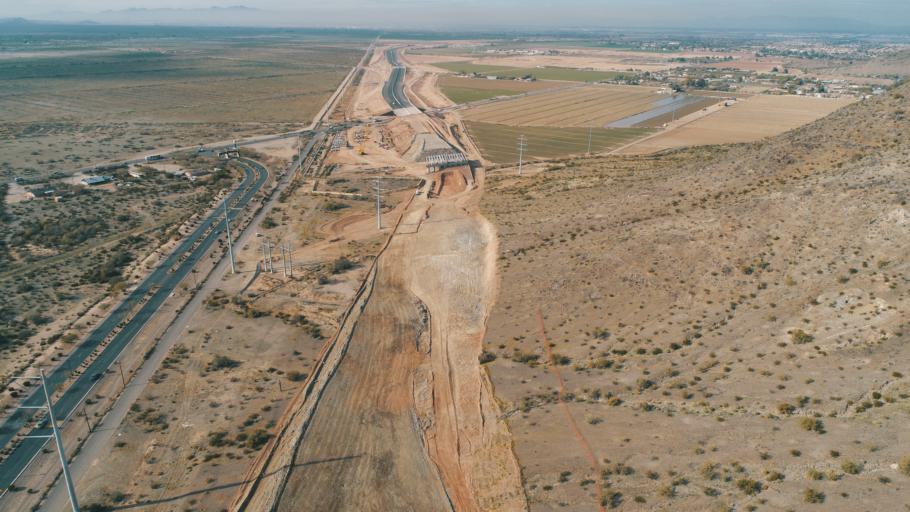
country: US
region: Arizona
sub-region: Maricopa County
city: Laveen
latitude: 33.3198
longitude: -112.1621
